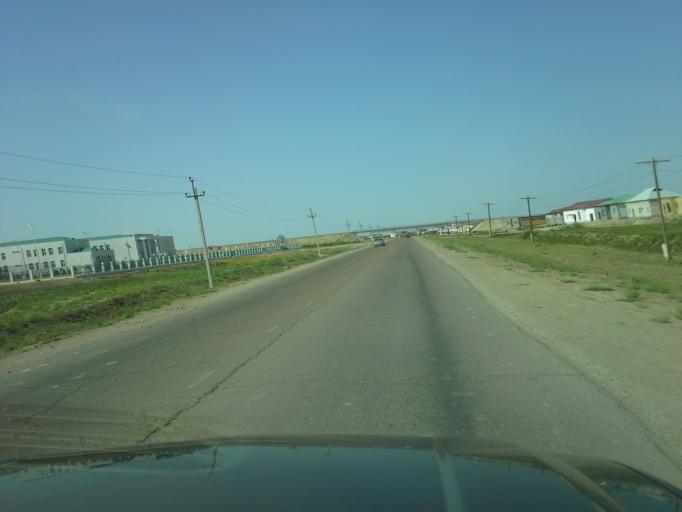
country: TM
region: Dasoguz
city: Dasoguz
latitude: 41.7963
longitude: 60.0184
